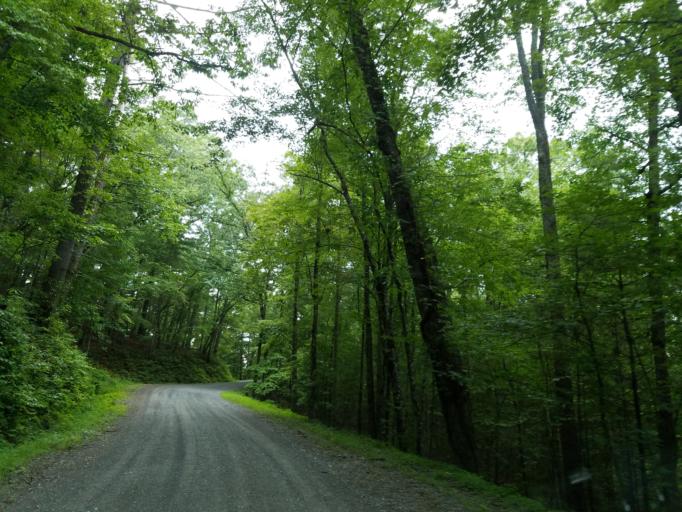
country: US
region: Georgia
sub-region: Fannin County
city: Blue Ridge
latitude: 34.8161
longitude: -84.2415
